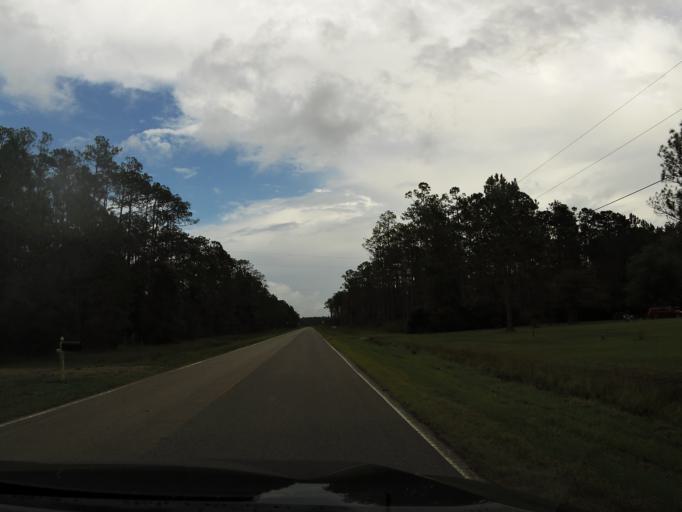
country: US
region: Florida
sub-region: Duval County
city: Baldwin
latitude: 30.4026
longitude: -82.0134
